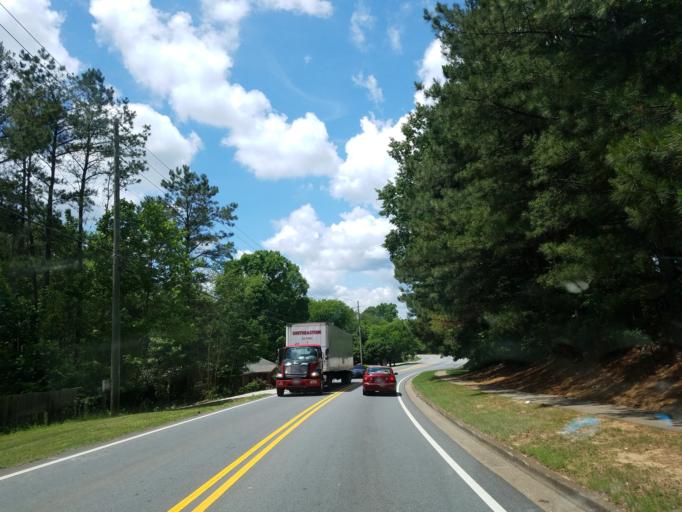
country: US
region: Georgia
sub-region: Cobb County
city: Kennesaw
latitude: 34.0335
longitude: -84.6406
